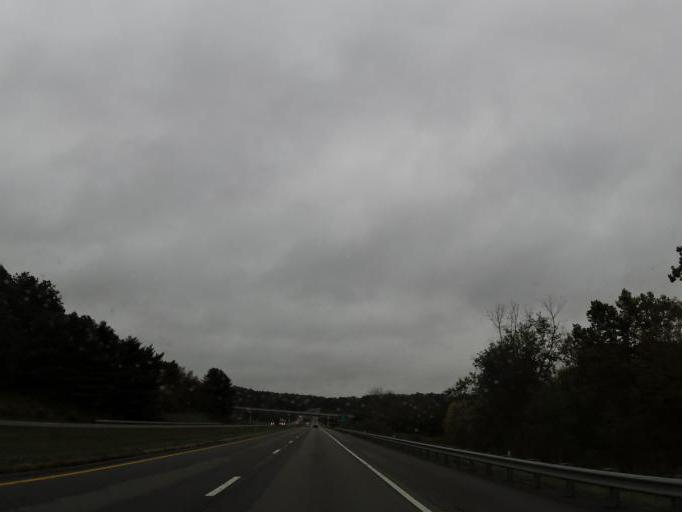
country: US
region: Virginia
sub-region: Wythe County
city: Wytheville
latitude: 36.9893
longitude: -81.0765
